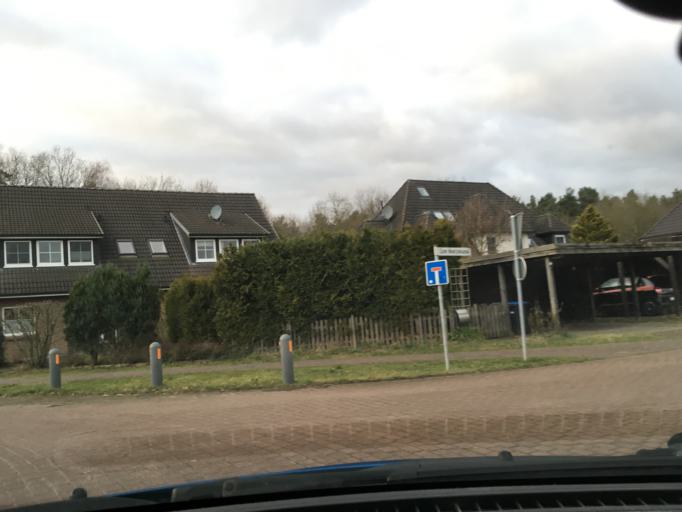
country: DE
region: Lower Saxony
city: Brietlingen
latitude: 53.3173
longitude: 10.4412
